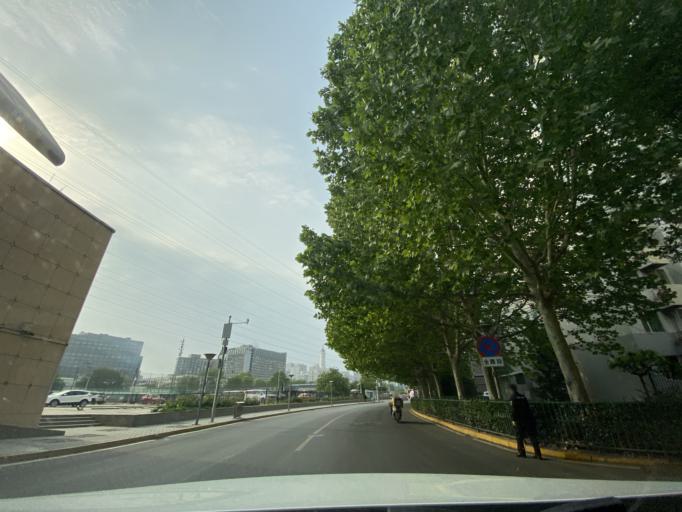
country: CN
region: Beijing
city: Haidian
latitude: 39.9763
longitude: 116.3358
